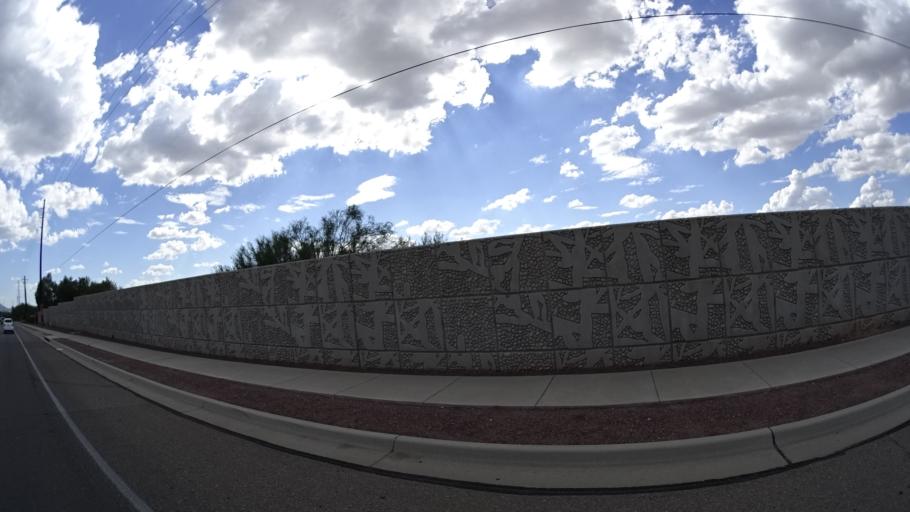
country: US
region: Arizona
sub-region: Pima County
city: Casas Adobes
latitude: 32.3317
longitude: -111.0130
